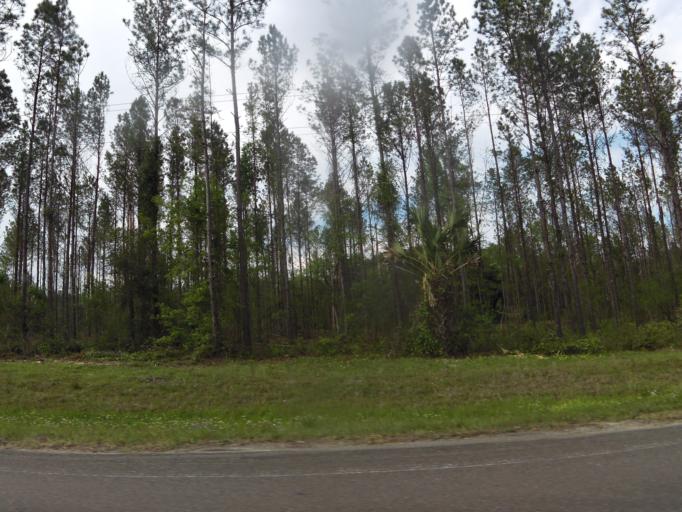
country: US
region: Georgia
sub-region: Camden County
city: Kingsland
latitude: 30.6990
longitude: -81.7701
